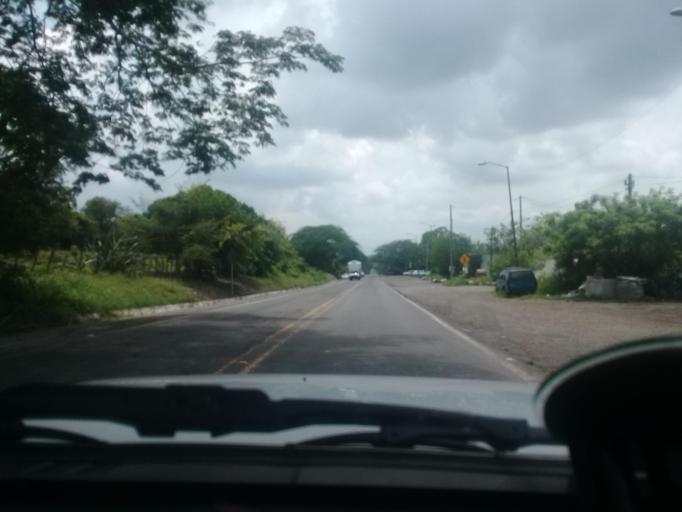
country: MX
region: Veracruz
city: Paso de Ovejas
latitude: 19.2906
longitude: -96.4467
